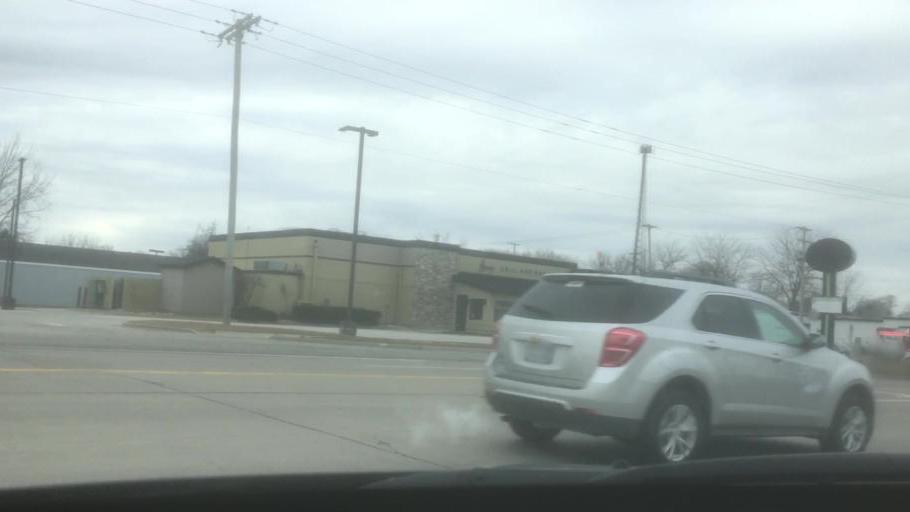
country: US
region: Michigan
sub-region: Bay County
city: Bay City
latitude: 43.6239
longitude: -83.8935
